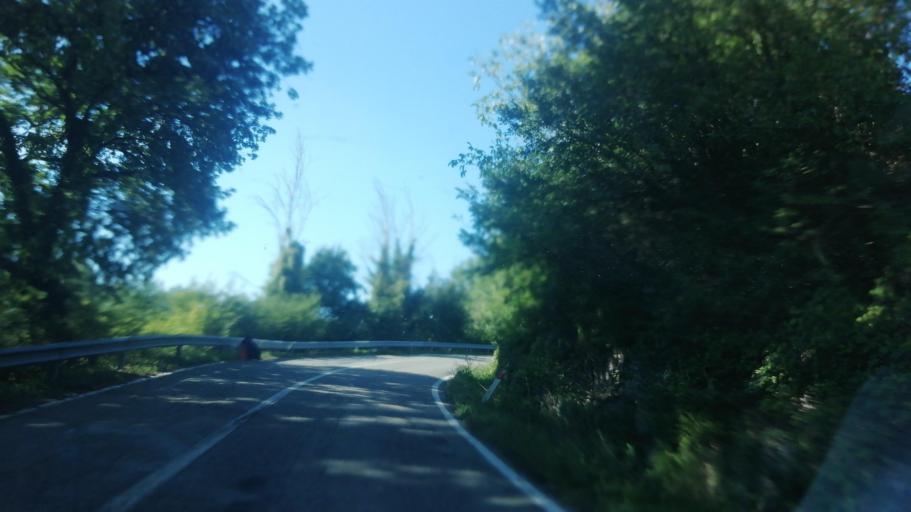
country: IT
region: The Marches
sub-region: Provincia di Pesaro e Urbino
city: Frontone
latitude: 43.5430
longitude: 12.7161
